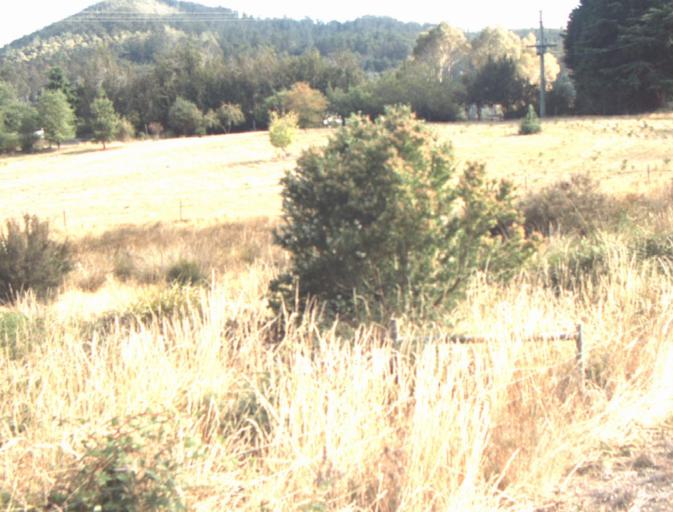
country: AU
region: Tasmania
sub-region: Launceston
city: Mayfield
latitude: -41.2947
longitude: 147.2034
